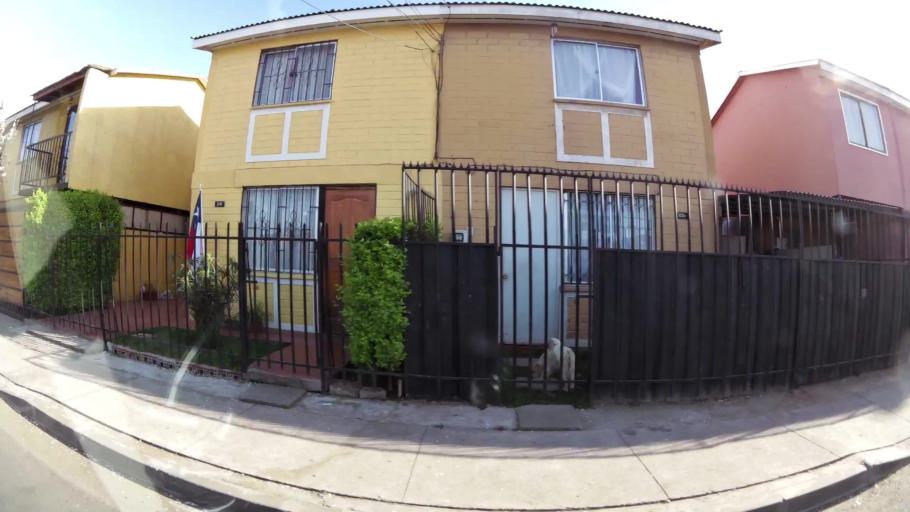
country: CL
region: Santiago Metropolitan
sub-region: Provincia de Cordillera
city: Puente Alto
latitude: -33.6122
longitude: -70.5948
